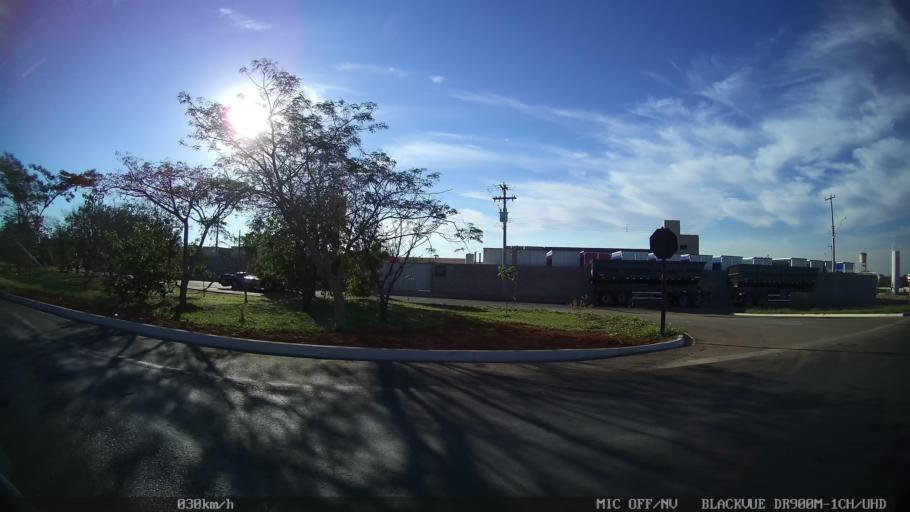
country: BR
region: Sao Paulo
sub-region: Americo Brasiliense
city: Americo Brasiliense
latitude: -21.7440
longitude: -48.1264
